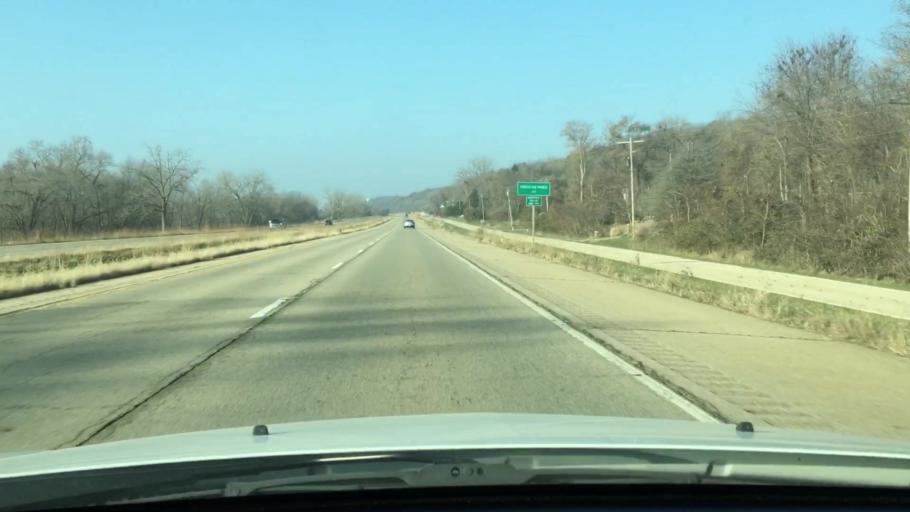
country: US
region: Illinois
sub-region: Peoria County
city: Glasford
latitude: 40.5603
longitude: -89.7586
